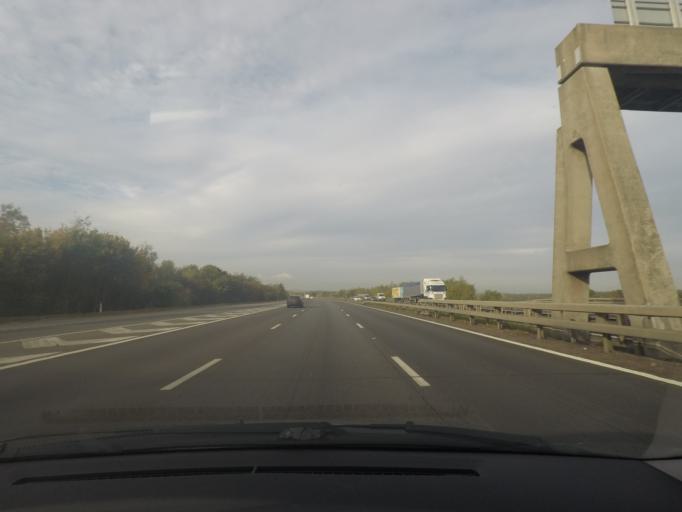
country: GB
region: England
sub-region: City and Borough of Leeds
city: Garforth
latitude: 53.8062
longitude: -1.3675
